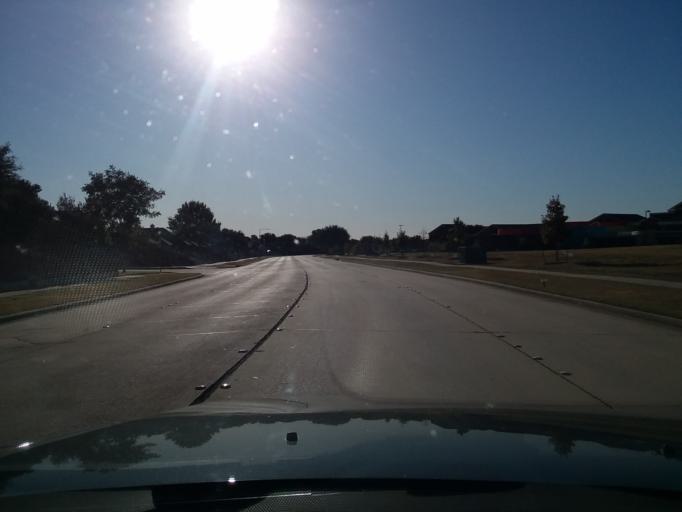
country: US
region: Texas
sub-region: Denton County
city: Lewisville
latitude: 33.0602
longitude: -97.0265
